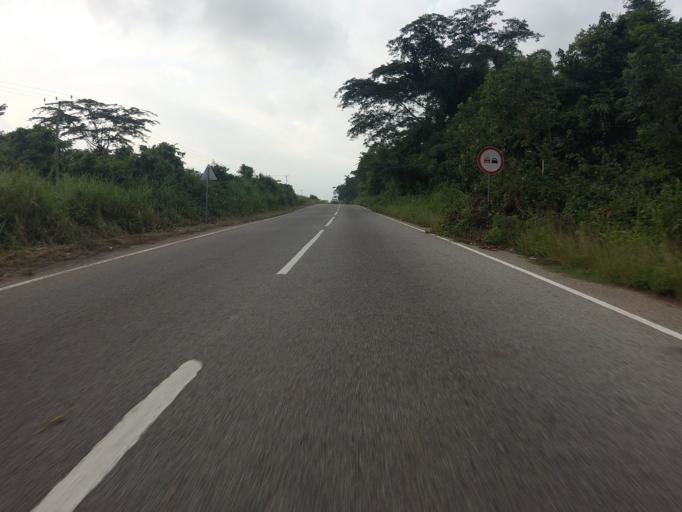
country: GH
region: Volta
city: Ho
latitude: 6.6440
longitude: 0.4691
